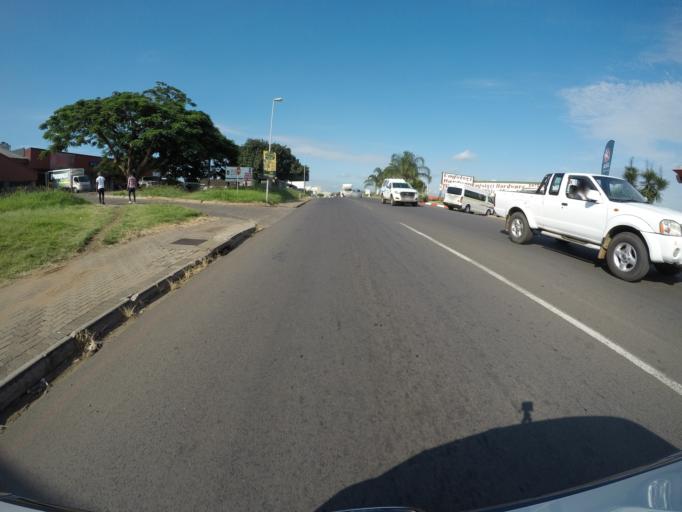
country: ZA
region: KwaZulu-Natal
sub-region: uThungulu District Municipality
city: Empangeni
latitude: -28.7728
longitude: 31.9031
